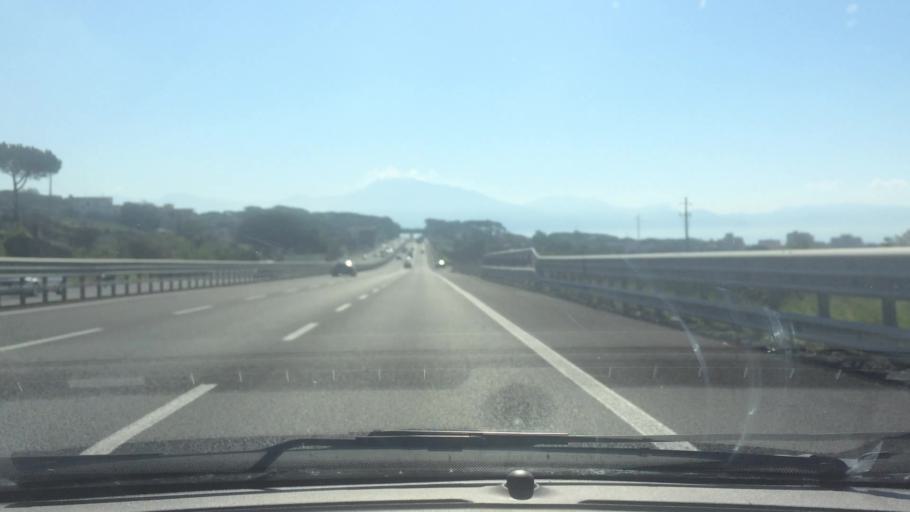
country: IT
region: Campania
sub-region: Provincia di Napoli
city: Ercolano
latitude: 40.8040
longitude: 14.3672
